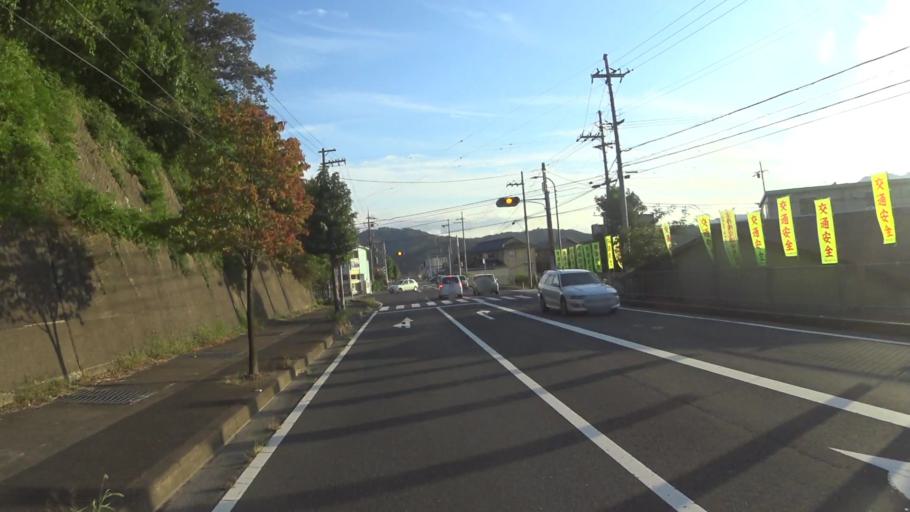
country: JP
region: Kyoto
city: Miyazu
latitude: 35.5791
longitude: 135.0995
